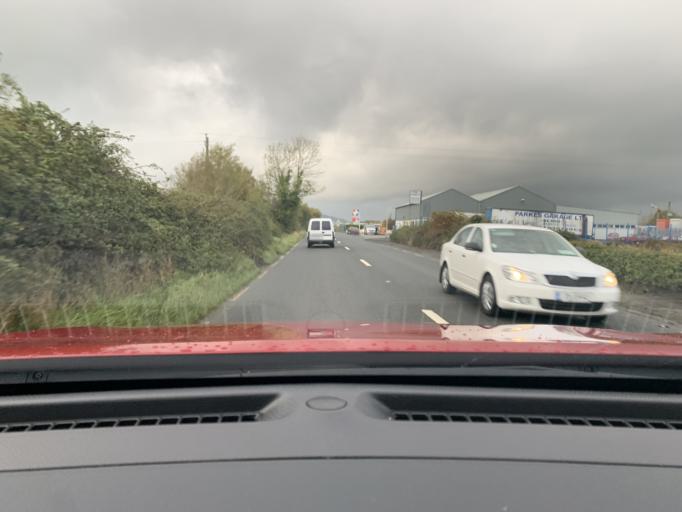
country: IE
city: Ballisodare
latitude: 54.2015
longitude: -8.5002
